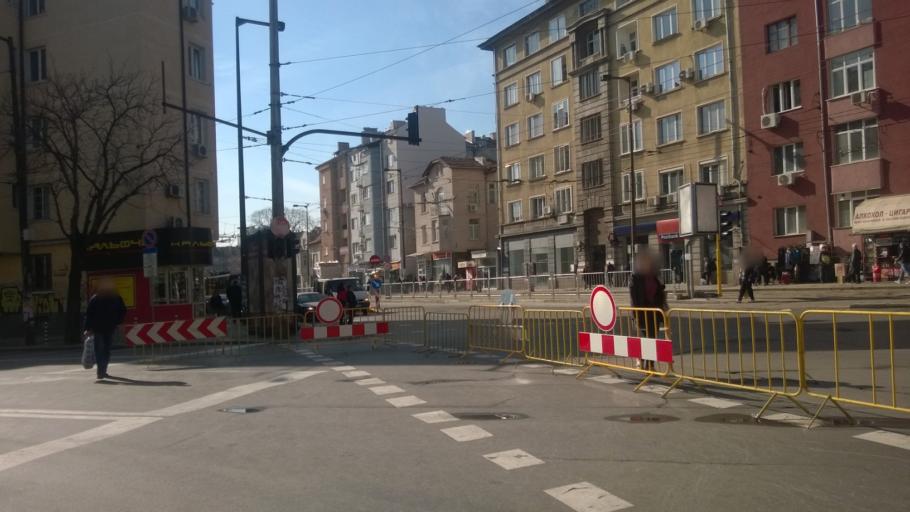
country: BG
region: Sofia-Capital
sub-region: Stolichna Obshtina
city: Sofia
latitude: 42.6894
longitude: 23.3141
